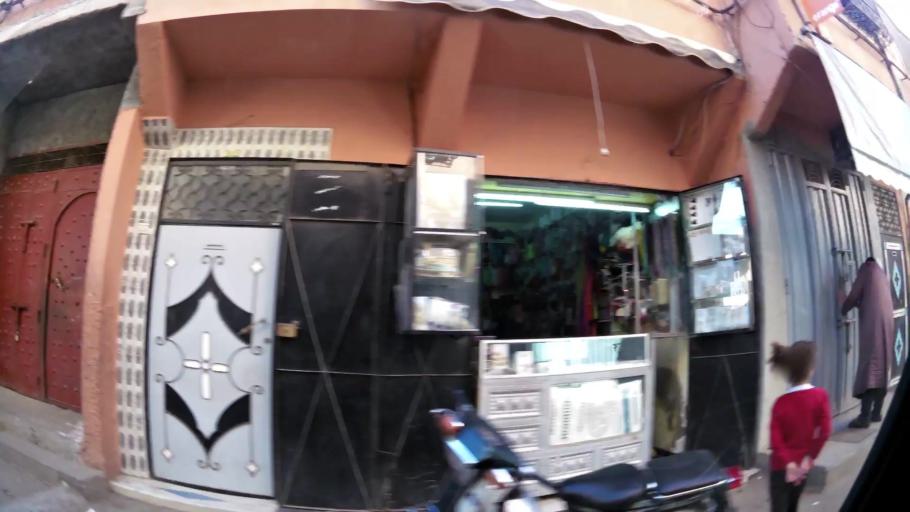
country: MA
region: Marrakech-Tensift-Al Haouz
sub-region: Marrakech
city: Marrakesh
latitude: 31.6131
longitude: -7.9654
